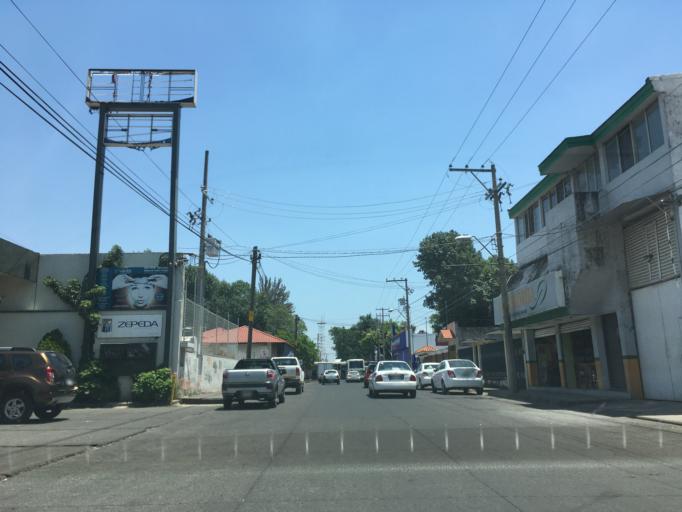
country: MX
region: Michoacan
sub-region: Uruapan
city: Uruapan
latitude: 19.4095
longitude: -102.0542
